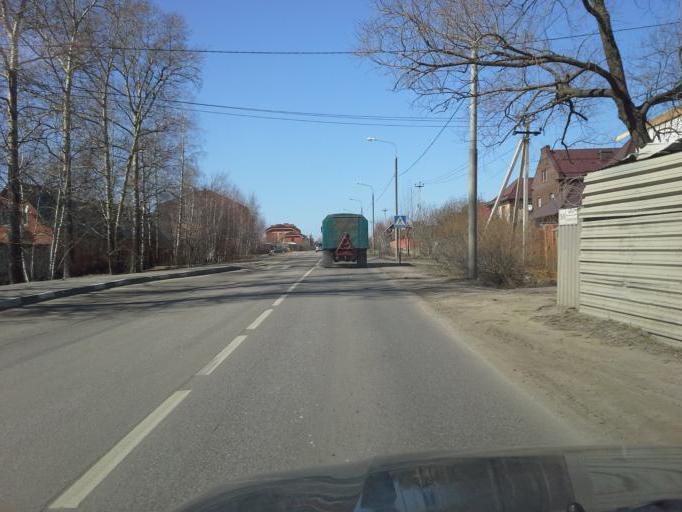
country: RU
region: Moscow
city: Vnukovo
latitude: 55.5988
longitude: 37.2022
